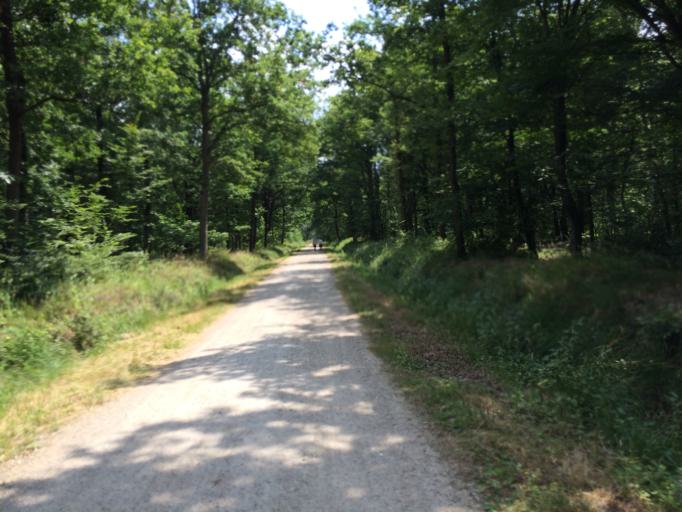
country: FR
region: Ile-de-France
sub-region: Departement de l'Essonne
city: Brunoy
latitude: 48.6756
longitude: 2.4914
